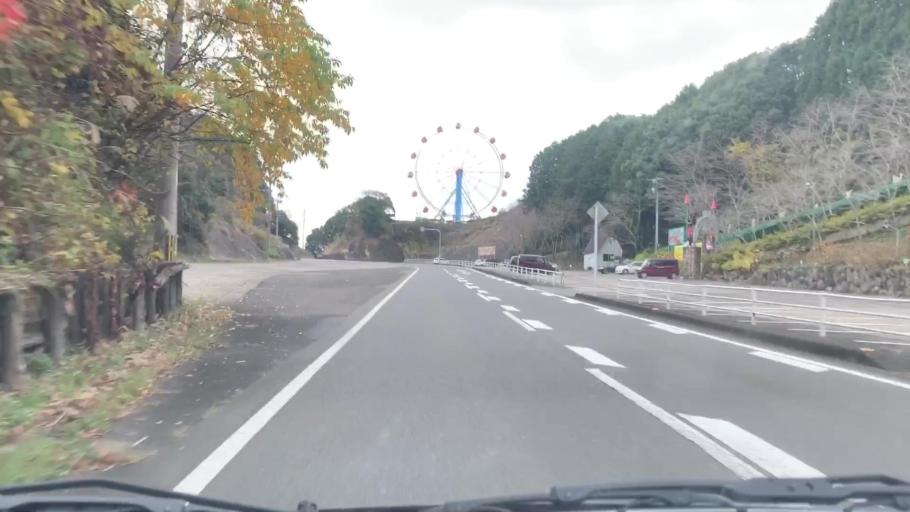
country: JP
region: Saga Prefecture
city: Ureshinomachi-shimojuku
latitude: 33.1315
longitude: 129.9740
